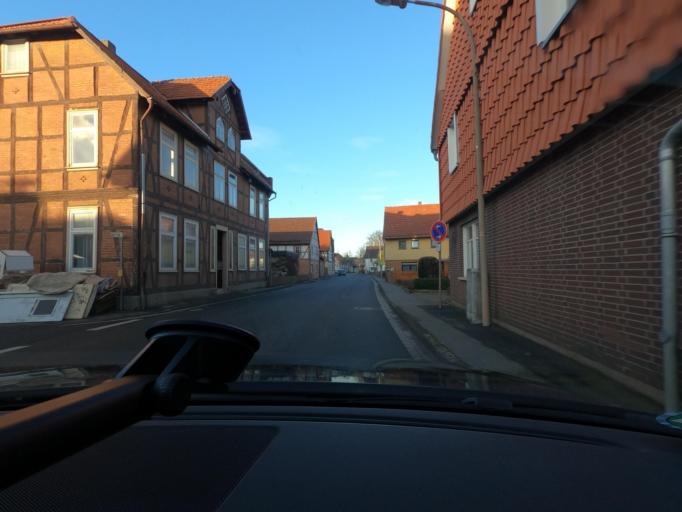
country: DE
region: Lower Saxony
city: Rhumspringe
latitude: 51.5610
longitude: 10.3106
